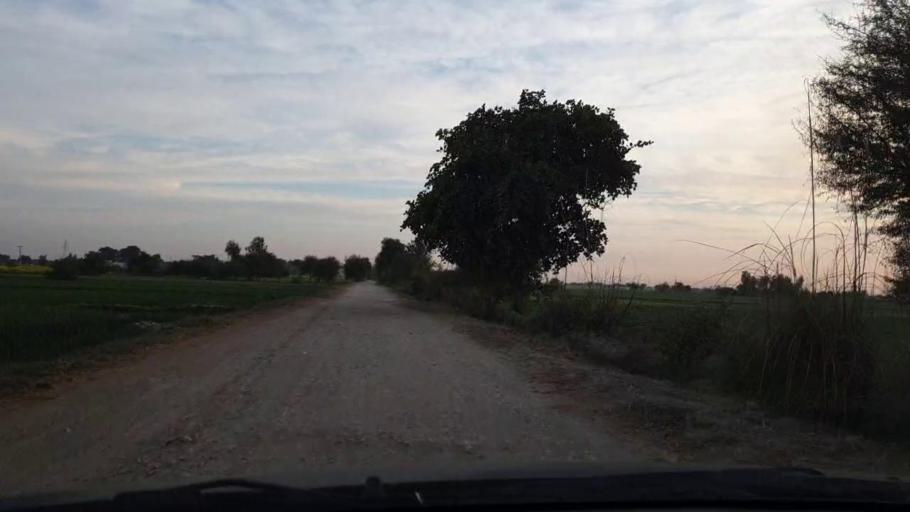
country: PK
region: Sindh
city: Khadro
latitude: 26.1237
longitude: 68.7780
